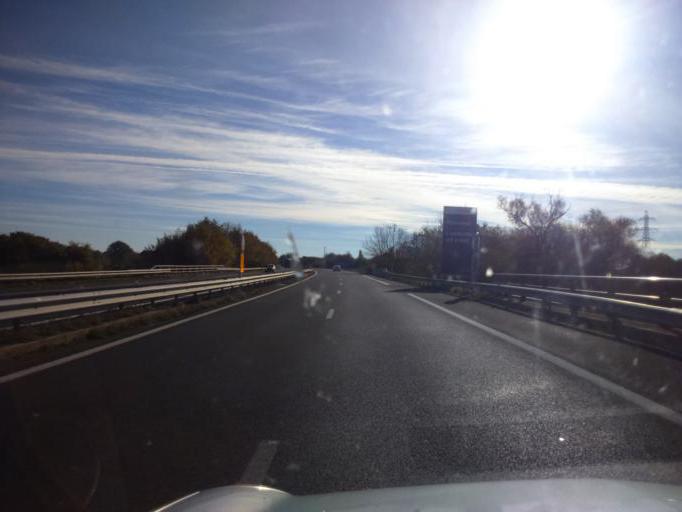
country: FR
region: Poitou-Charentes
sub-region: Departement de la Charente-Maritime
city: Breuil-Magne
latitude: 45.9682
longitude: -0.9809
